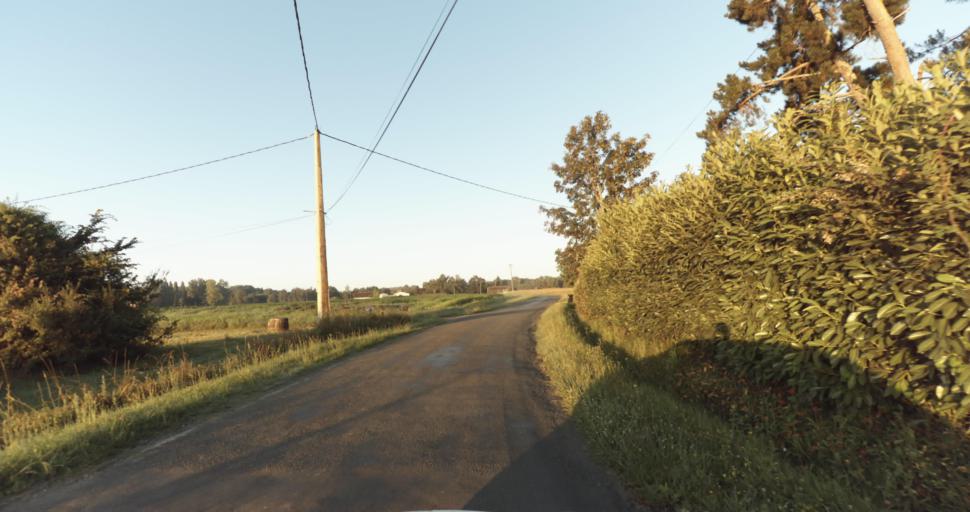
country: FR
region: Aquitaine
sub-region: Departement de la Gironde
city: Bazas
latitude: 44.4282
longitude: -0.2038
